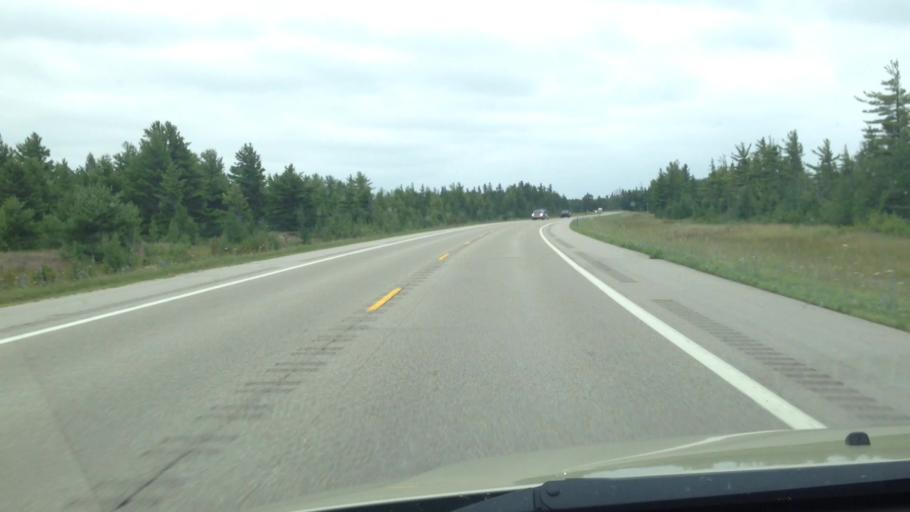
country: US
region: Michigan
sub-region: Mackinac County
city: Saint Ignace
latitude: 45.9217
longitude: -84.8772
